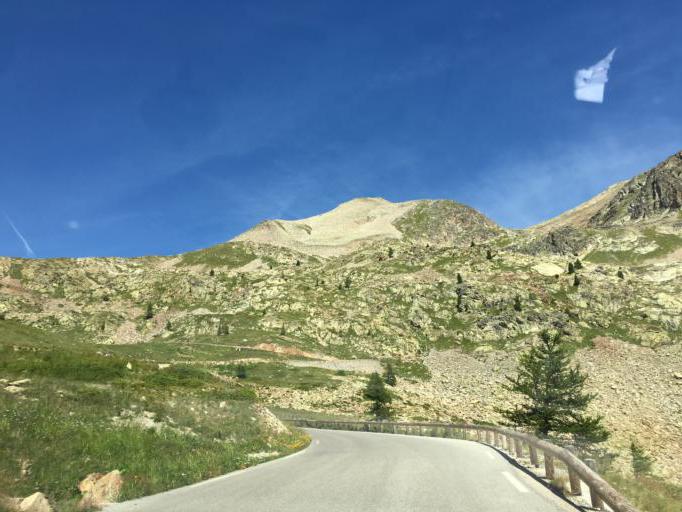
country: IT
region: Piedmont
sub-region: Provincia di Cuneo
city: Vinadio
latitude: 44.1983
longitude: 7.1550
